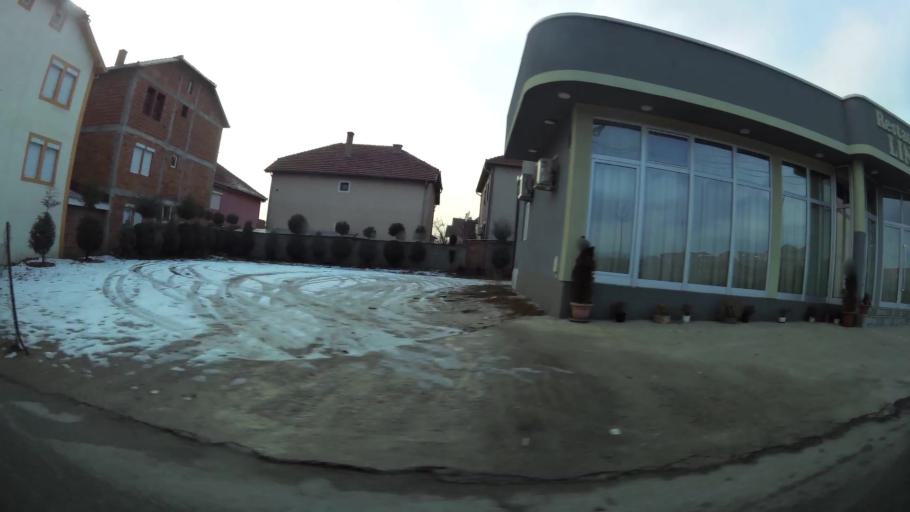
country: MK
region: Aracinovo
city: Arachinovo
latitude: 42.0265
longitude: 21.5733
